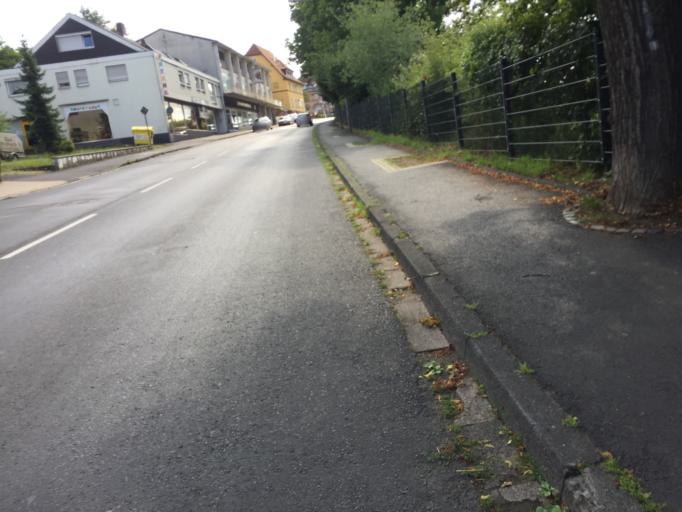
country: DE
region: Hesse
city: Schwalmstadt
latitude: 50.9117
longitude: 9.1911
